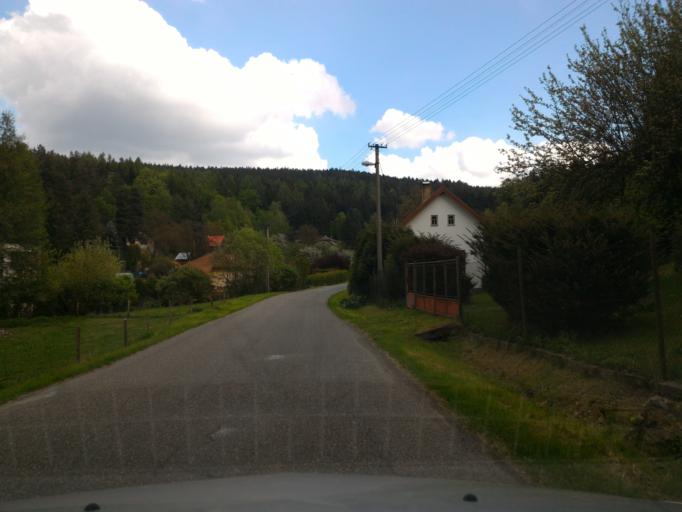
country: CZ
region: Vysocina
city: Ledec nad Sazavou
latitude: 49.6446
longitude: 15.2974
